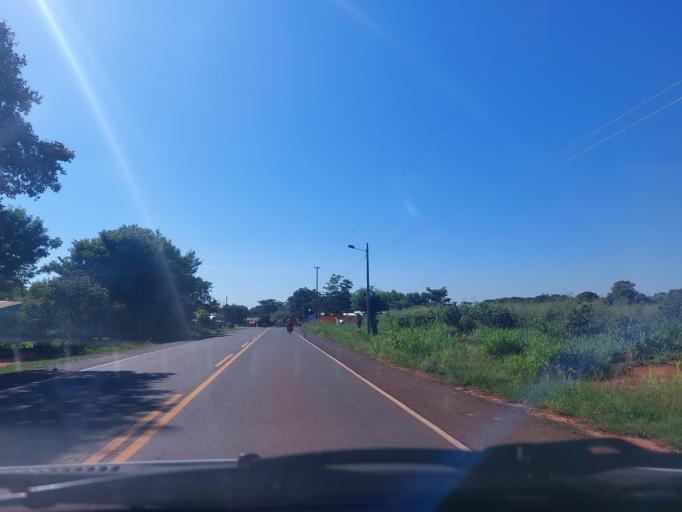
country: PY
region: San Pedro
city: Guayaybi
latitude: -24.3157
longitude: -56.1625
